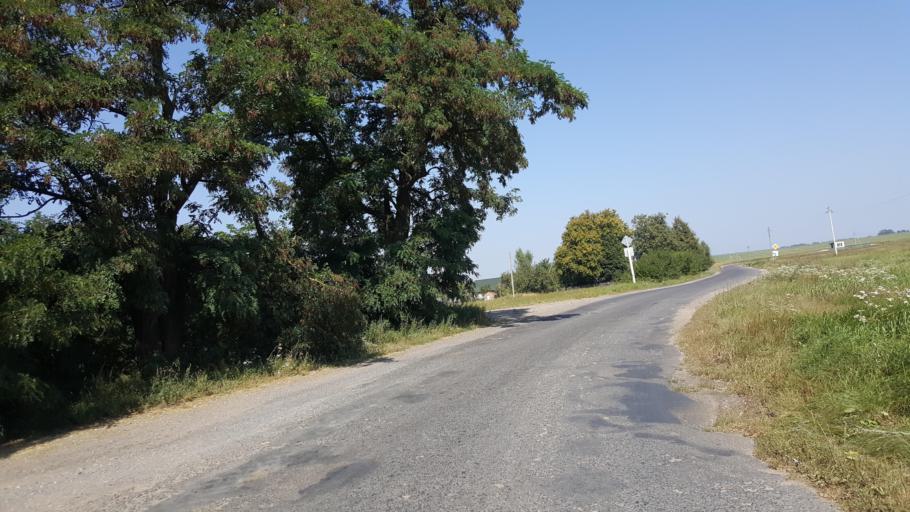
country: BY
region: Brest
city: Vysokaye
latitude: 52.4461
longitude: 23.4590
